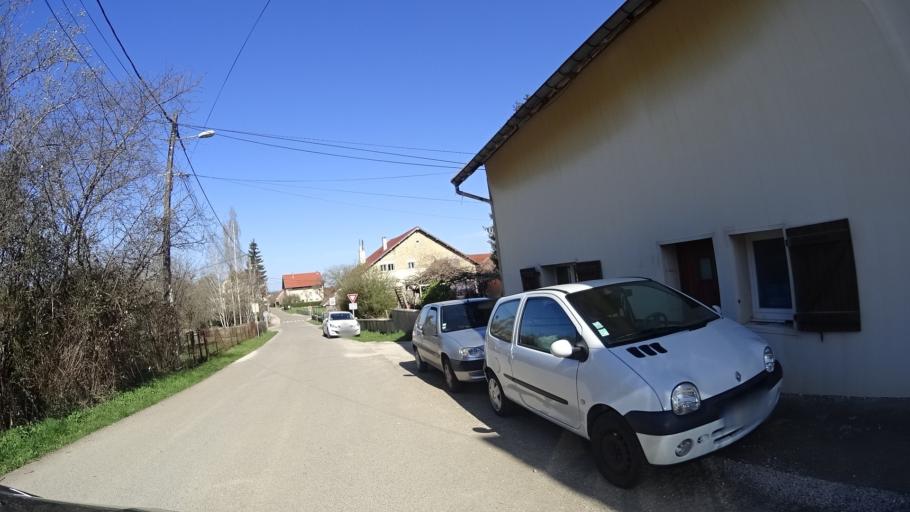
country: FR
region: Franche-Comte
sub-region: Departement du Doubs
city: Ornans
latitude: 47.1433
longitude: 6.0895
